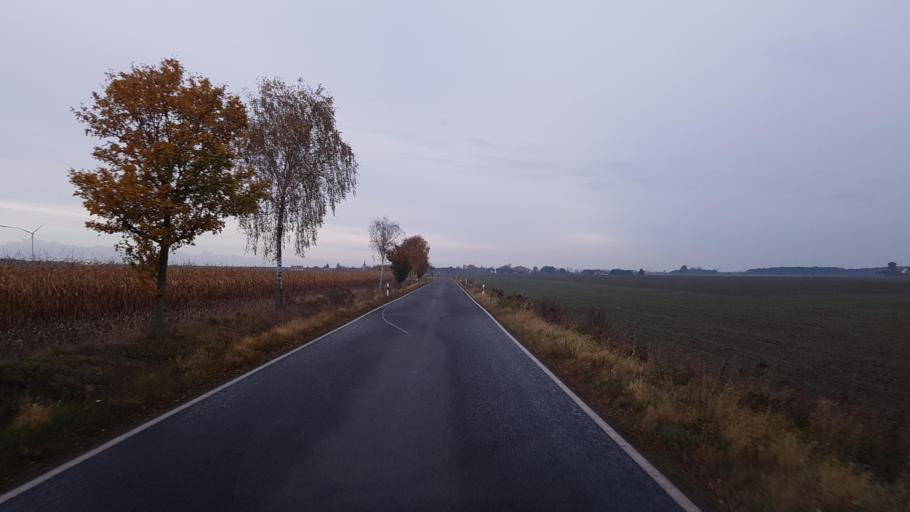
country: DE
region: Saxony-Anhalt
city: Seyda
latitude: 51.9193
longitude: 12.9029
